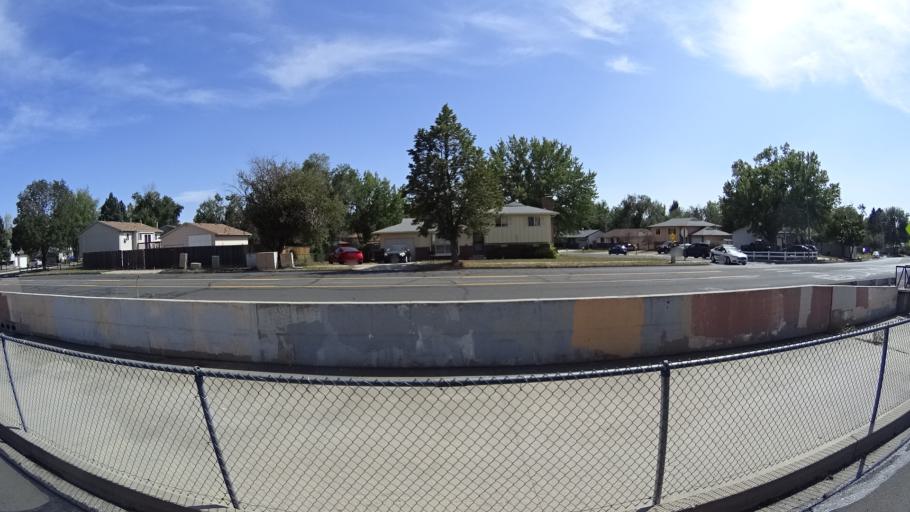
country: US
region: Colorado
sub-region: El Paso County
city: Cimarron Hills
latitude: 38.8999
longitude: -104.7596
